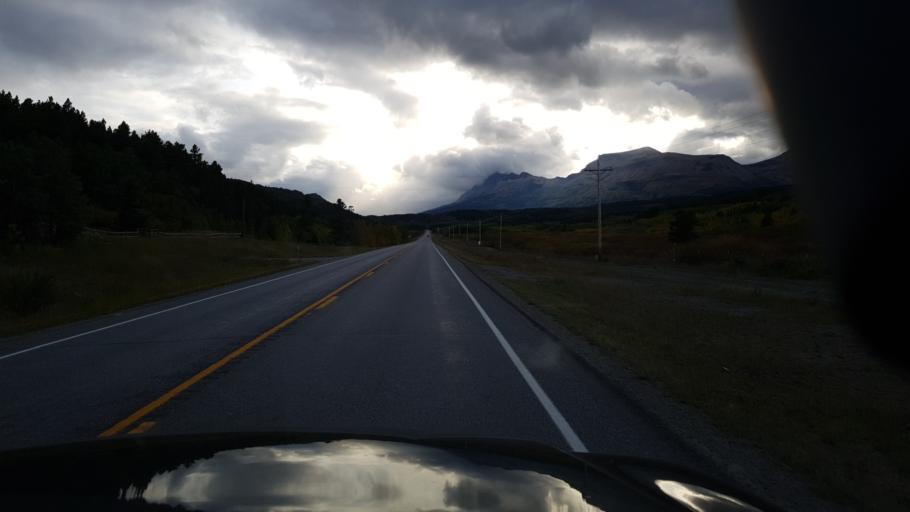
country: US
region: Montana
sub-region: Glacier County
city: South Browning
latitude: 48.4152
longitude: -113.2253
